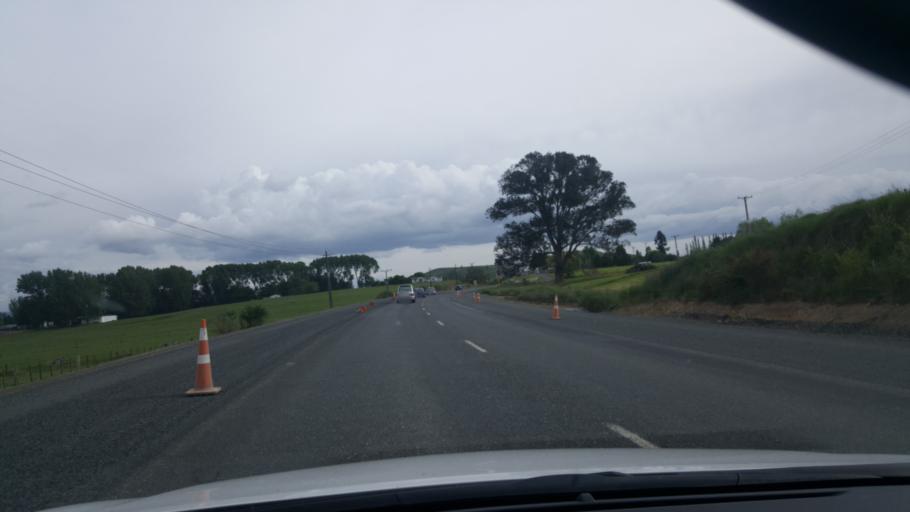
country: NZ
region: Bay of Plenty
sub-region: Rotorua District
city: Rotorua
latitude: -38.4185
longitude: 176.3190
